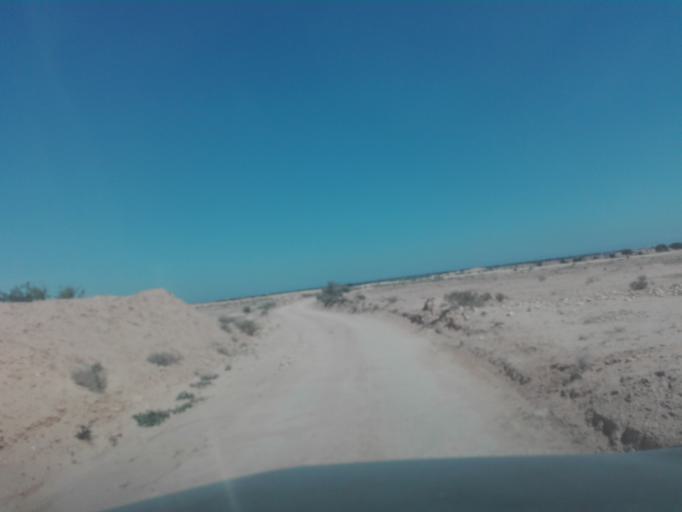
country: TN
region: Qabis
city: Gabes
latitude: 33.8503
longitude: 10.0002
